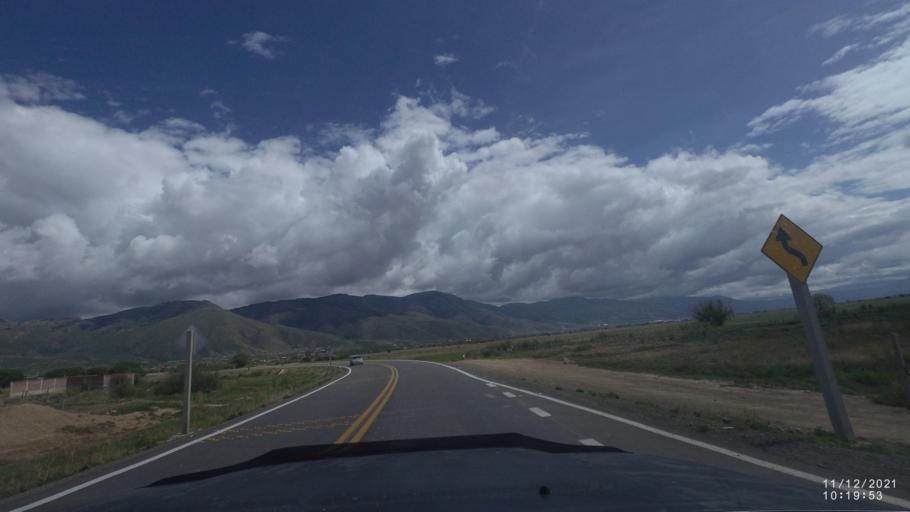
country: BO
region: Cochabamba
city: Tarata
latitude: -17.5638
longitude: -66.0078
